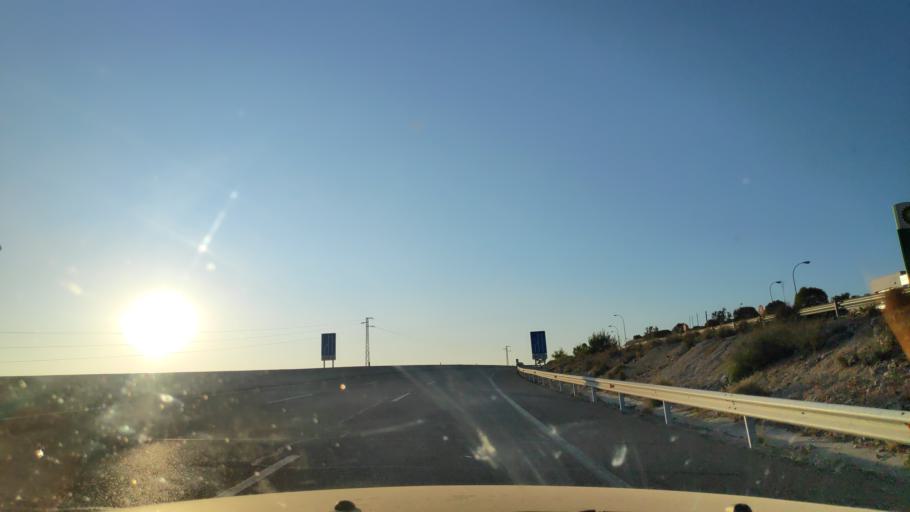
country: ES
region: Madrid
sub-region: Provincia de Madrid
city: Perales de Tajuna
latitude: 40.2490
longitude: -3.3502
